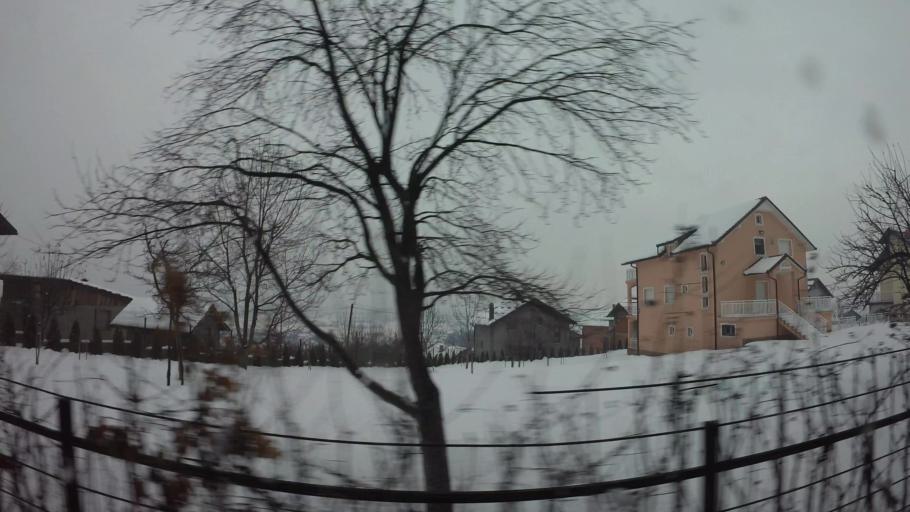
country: BA
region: Federation of Bosnia and Herzegovina
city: Hadzici
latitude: 43.8472
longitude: 18.2713
